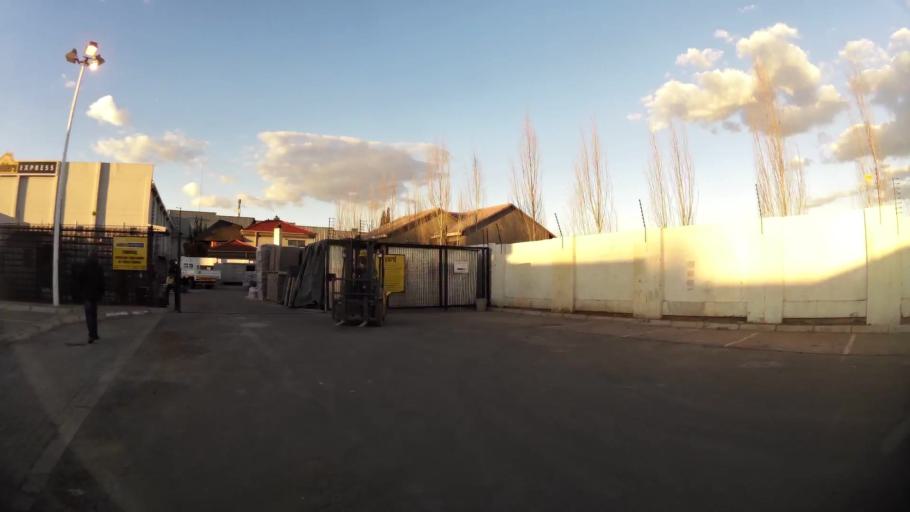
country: ZA
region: North-West
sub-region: Dr Kenneth Kaunda District Municipality
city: Potchefstroom
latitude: -26.7138
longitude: 27.1084
